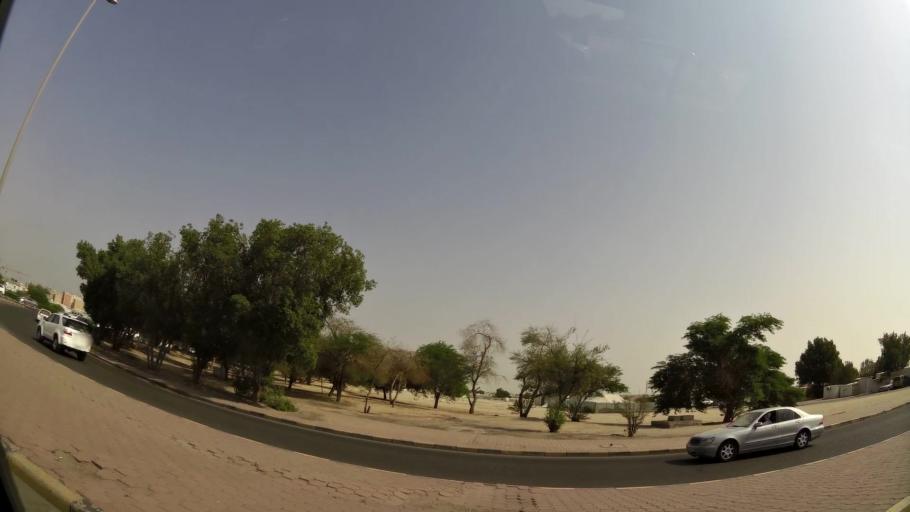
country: KW
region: Muhafazat al Jahra'
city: Al Jahra'
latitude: 29.3353
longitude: 47.6662
